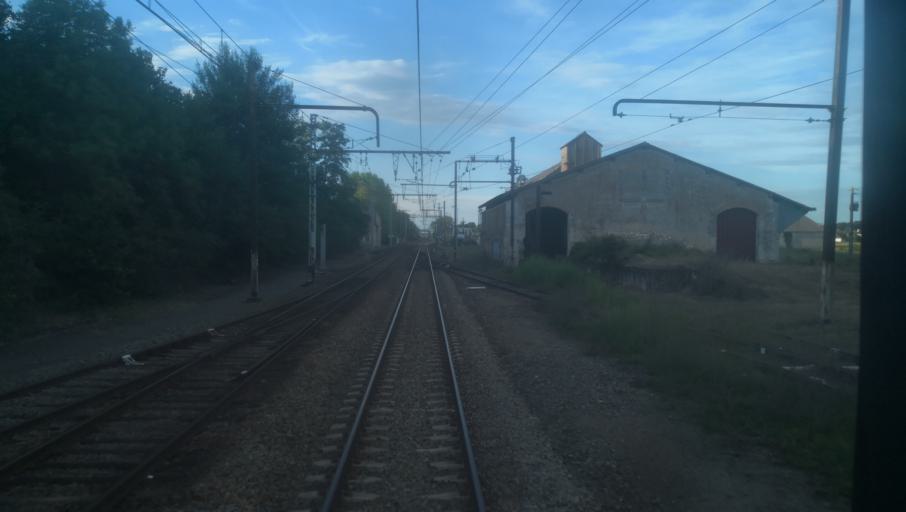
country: FR
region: Centre
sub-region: Departement de l'Indre
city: Luant
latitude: 46.6932
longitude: 1.5619
